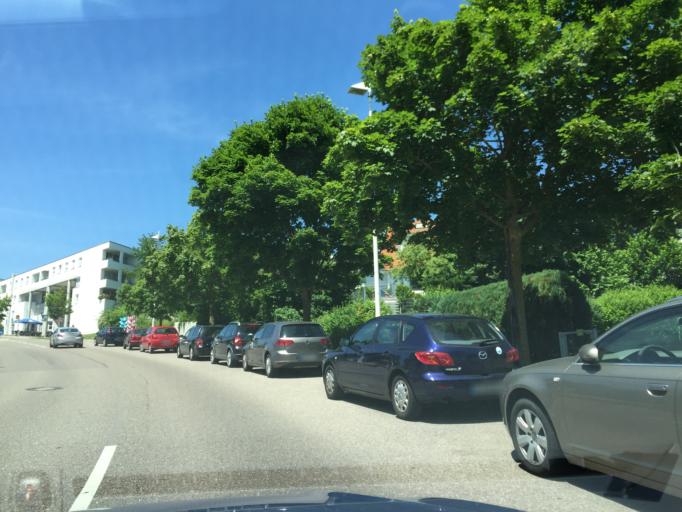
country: DE
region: Baden-Wuerttemberg
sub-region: Tuebingen Region
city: Ulm
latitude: 48.4132
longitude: 9.9511
